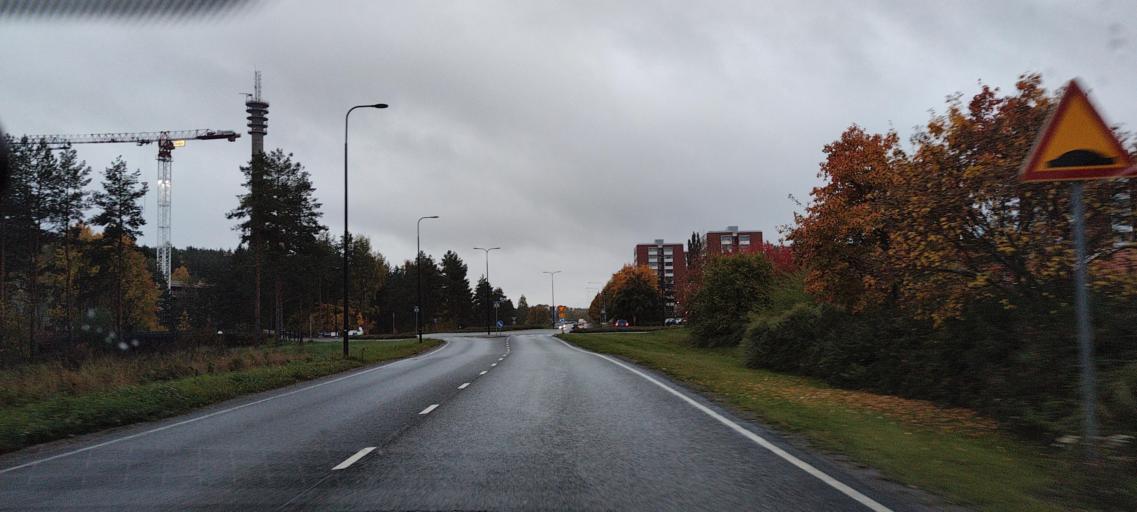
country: FI
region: Varsinais-Suomi
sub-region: Turku
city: Kaarina
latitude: 60.4518
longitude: 22.3314
